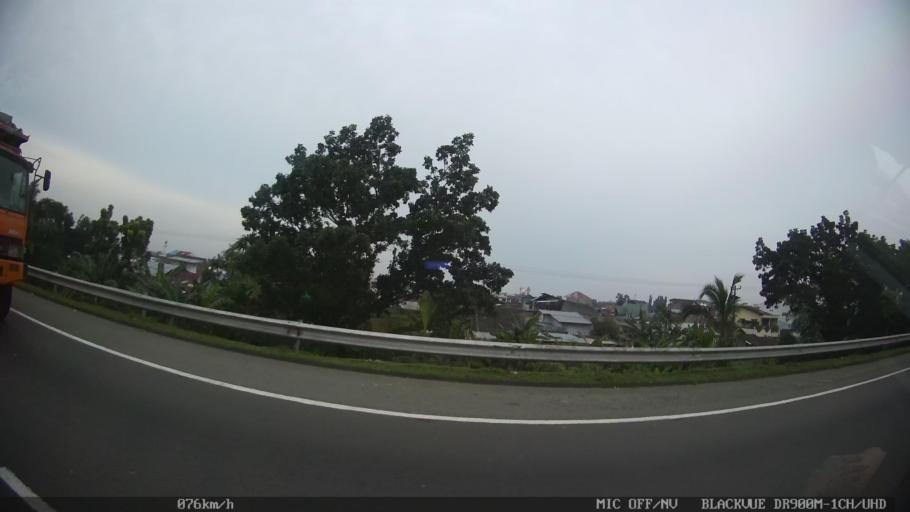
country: ID
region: North Sumatra
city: Medan
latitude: 3.5862
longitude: 98.7241
